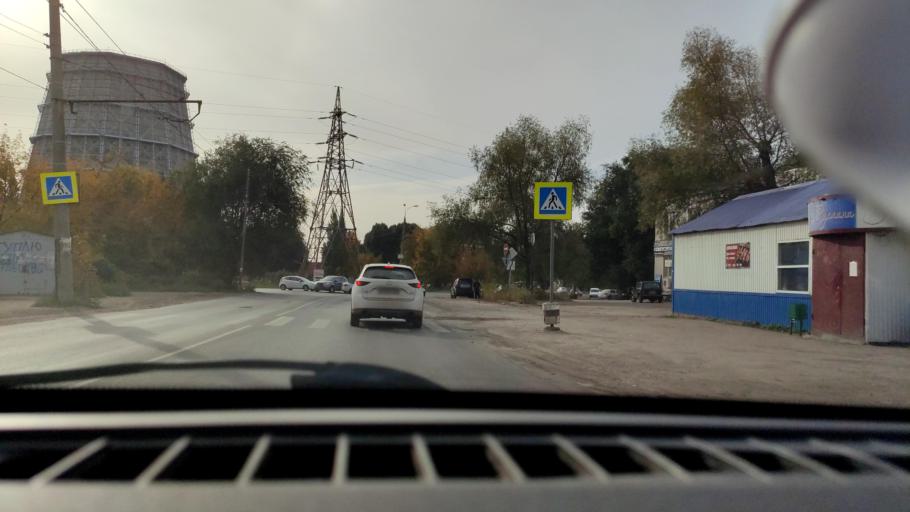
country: RU
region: Samara
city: Petra-Dubrava
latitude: 53.2519
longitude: 50.2676
